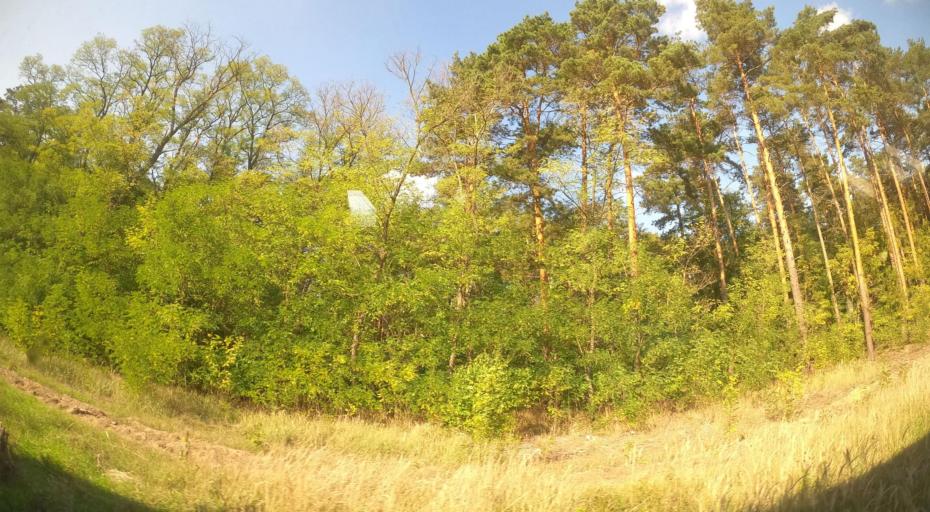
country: PL
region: Lubusz
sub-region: Zielona Gora
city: Zielona Gora
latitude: 51.9393
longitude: 15.4432
